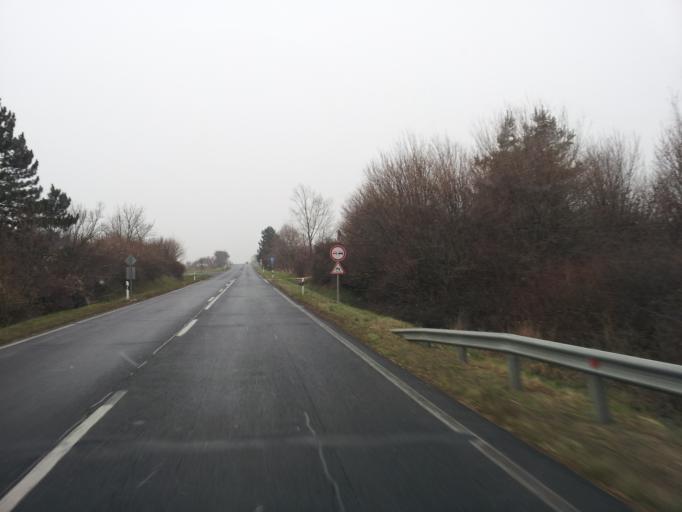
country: HU
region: Veszprem
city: Urkut
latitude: 47.1529
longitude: 17.6485
